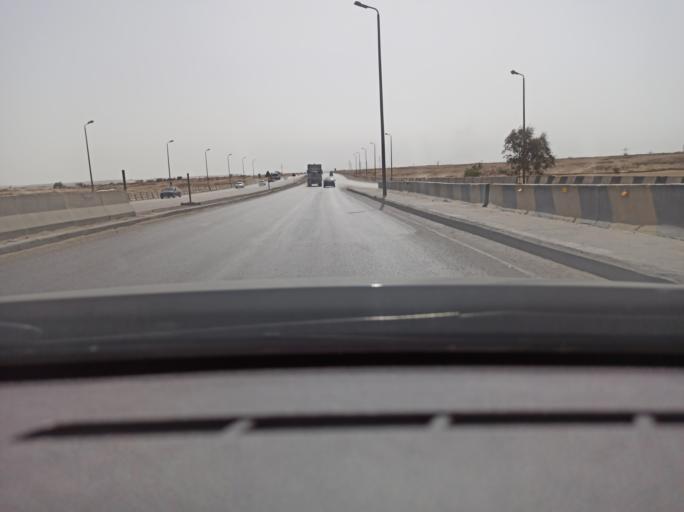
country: EG
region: Muhafazat al Qahirah
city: Halwan
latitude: 29.7889
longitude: 31.3481
